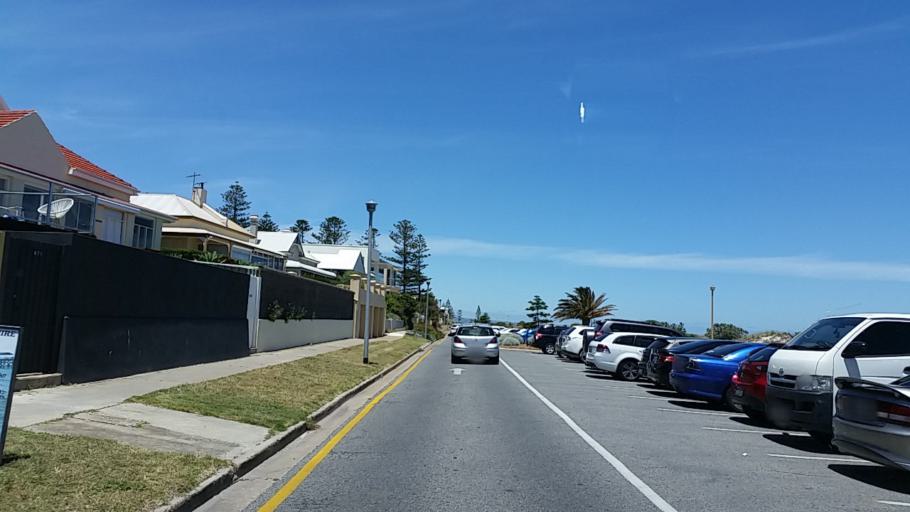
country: AU
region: South Australia
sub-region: Charles Sturt
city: Grange
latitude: -34.9037
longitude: 138.4896
